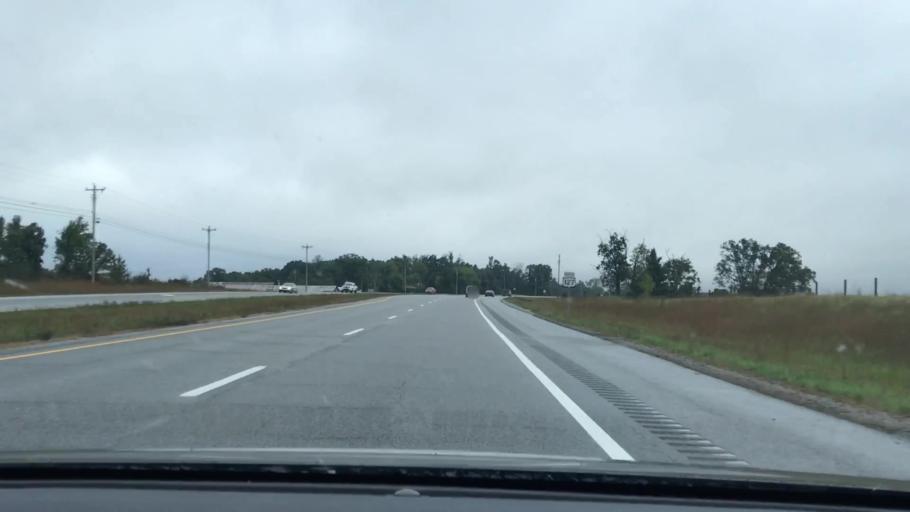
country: US
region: Tennessee
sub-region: Fentress County
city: Grimsley
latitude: 36.3078
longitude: -84.9746
